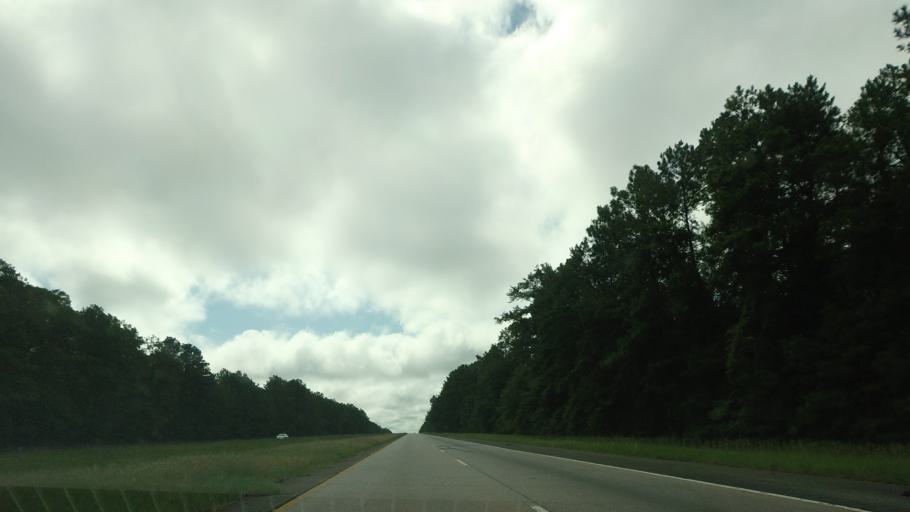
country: US
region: Georgia
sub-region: Houston County
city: Robins Air Force Base
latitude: 32.7060
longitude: -83.5146
